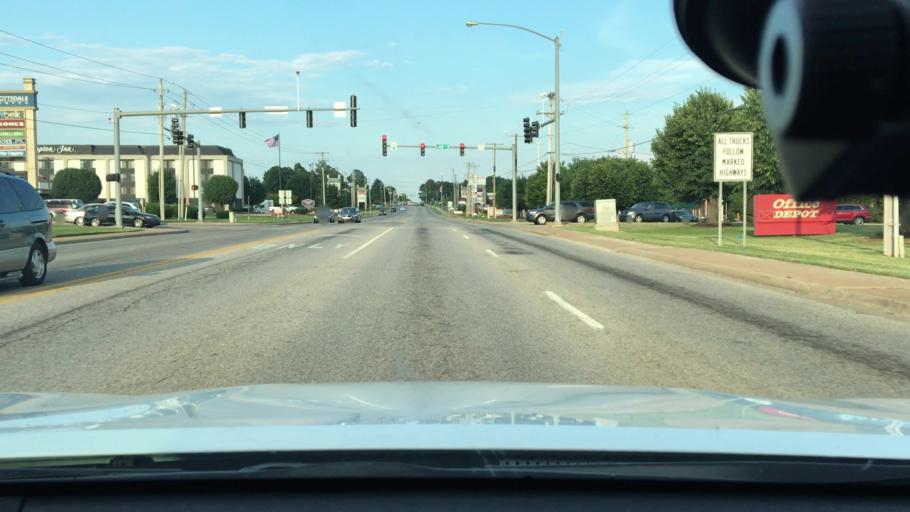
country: US
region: Arkansas
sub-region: Benton County
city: Bentonville
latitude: 36.3350
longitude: -94.1815
